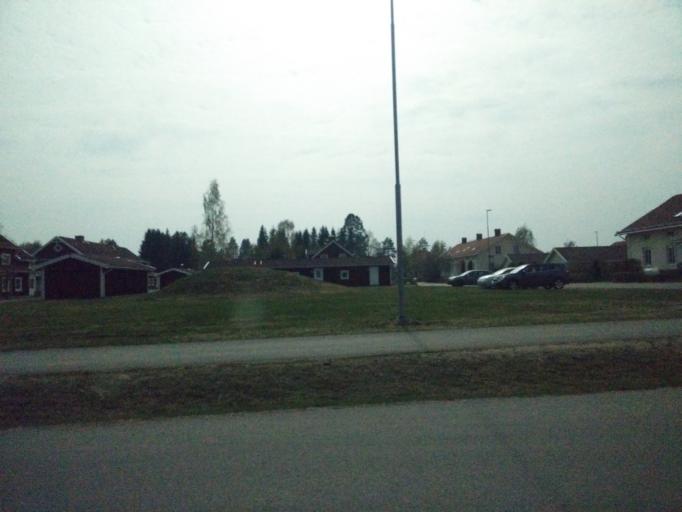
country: SE
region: Vaermland
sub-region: Munkfors Kommun
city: Munkfors
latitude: 59.8404
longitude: 13.5430
